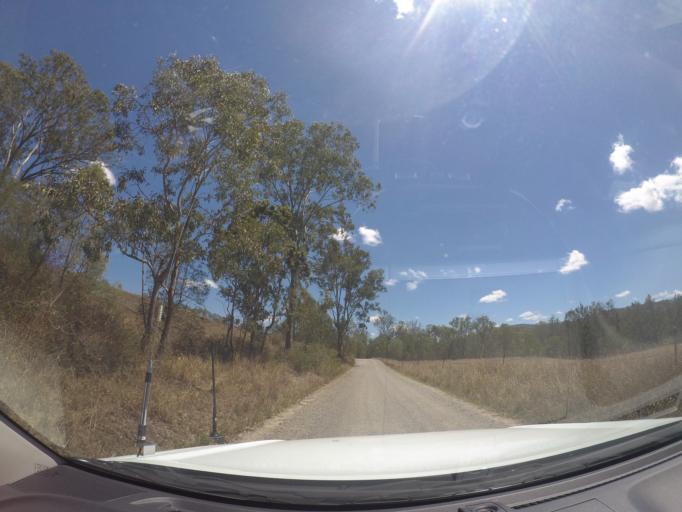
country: AU
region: Queensland
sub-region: Logan
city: North Maclean
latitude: -27.8235
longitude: 152.8594
